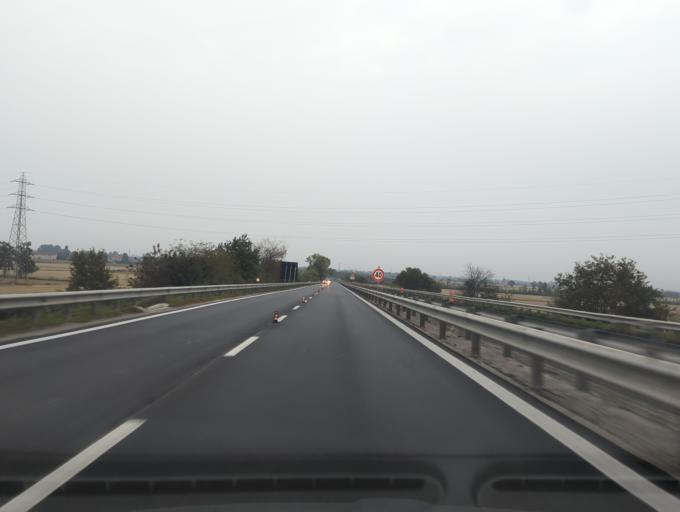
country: IT
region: Piedmont
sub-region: Provincia di Novara
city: Novara
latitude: 45.4259
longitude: 8.6522
